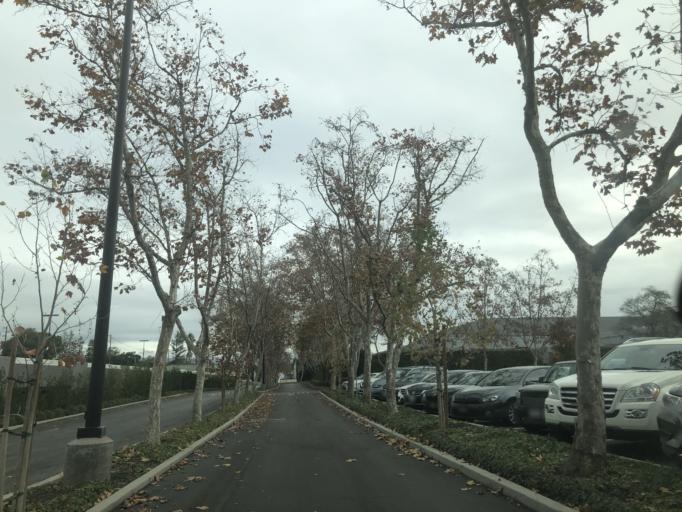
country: US
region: California
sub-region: Santa Clara County
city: Santa Clara
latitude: 37.3769
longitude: -121.9899
